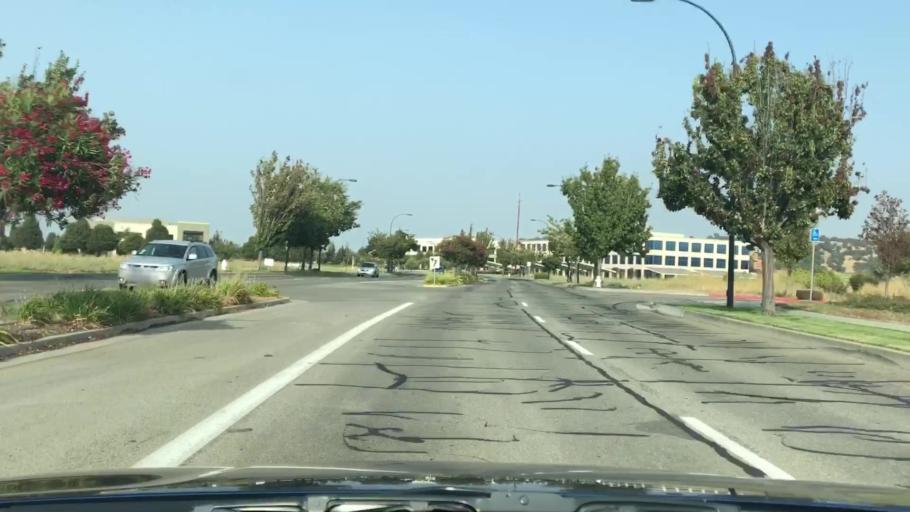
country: US
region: California
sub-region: Solano County
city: Green Valley
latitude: 38.2211
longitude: -122.1371
